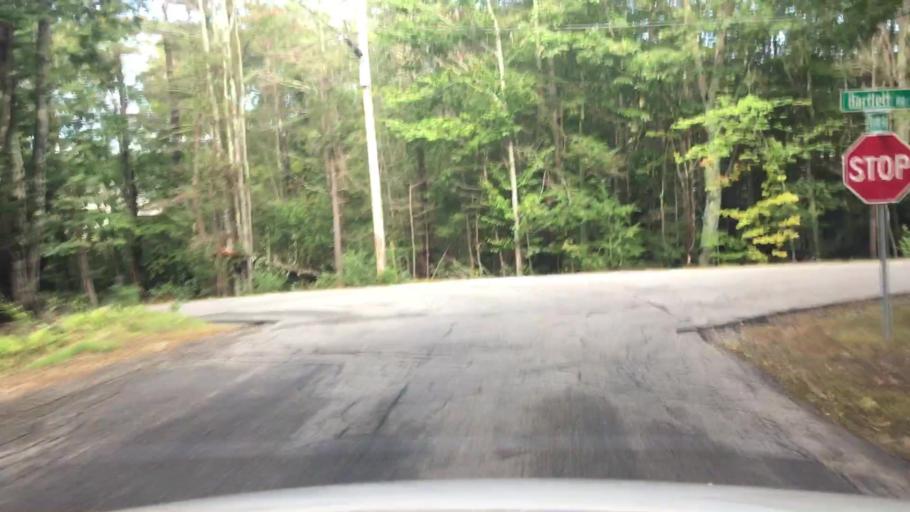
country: US
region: Maine
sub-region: York County
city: York Harbor
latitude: 43.1192
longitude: -70.6791
